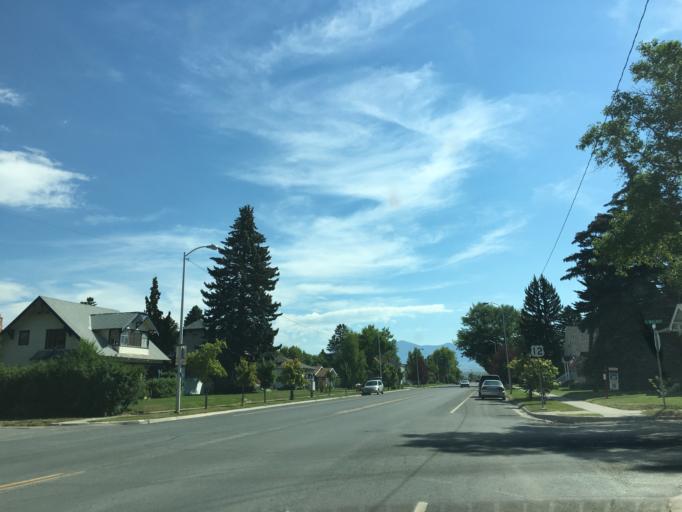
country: US
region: Montana
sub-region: Broadwater County
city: Townsend
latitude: 46.3212
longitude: -111.5150
